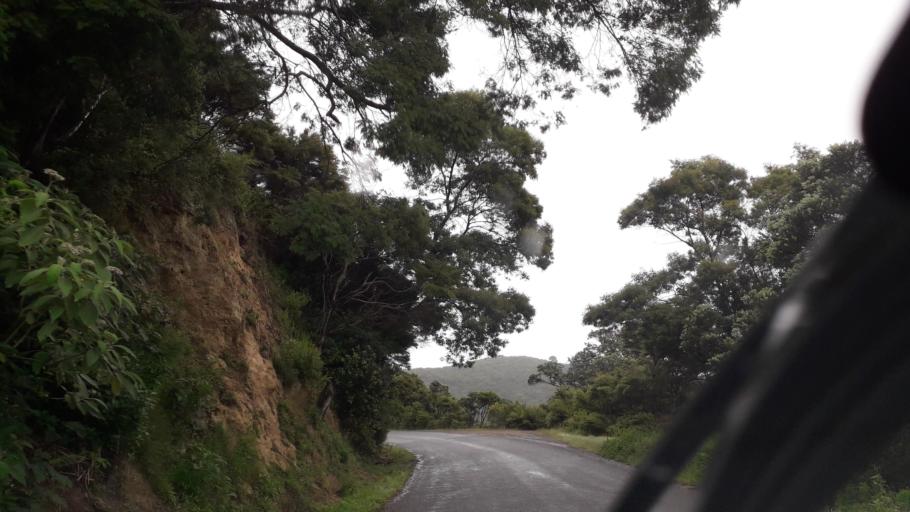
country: NZ
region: Northland
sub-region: Far North District
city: Paihia
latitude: -35.2328
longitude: 174.2608
